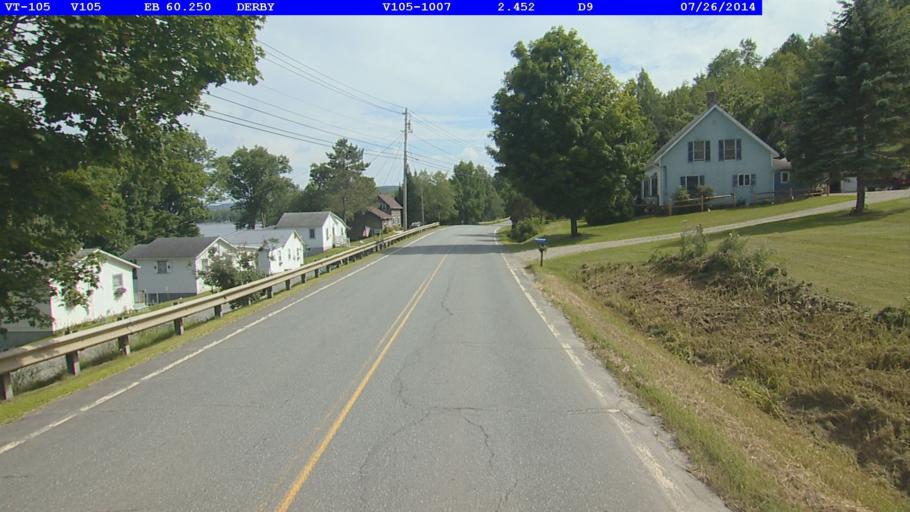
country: US
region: Vermont
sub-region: Orleans County
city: Newport
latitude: 44.9263
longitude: -72.1111
